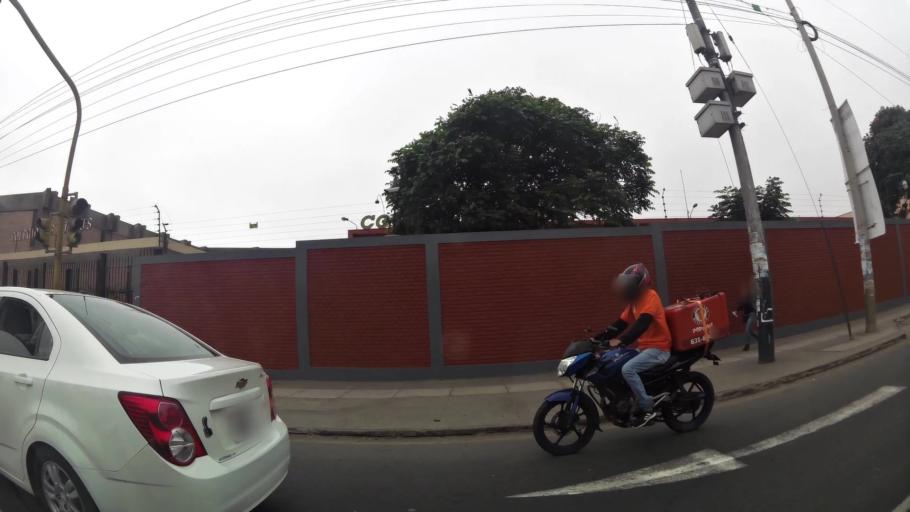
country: PE
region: Lima
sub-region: Lima
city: San Isidro
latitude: -12.0825
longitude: -77.0600
